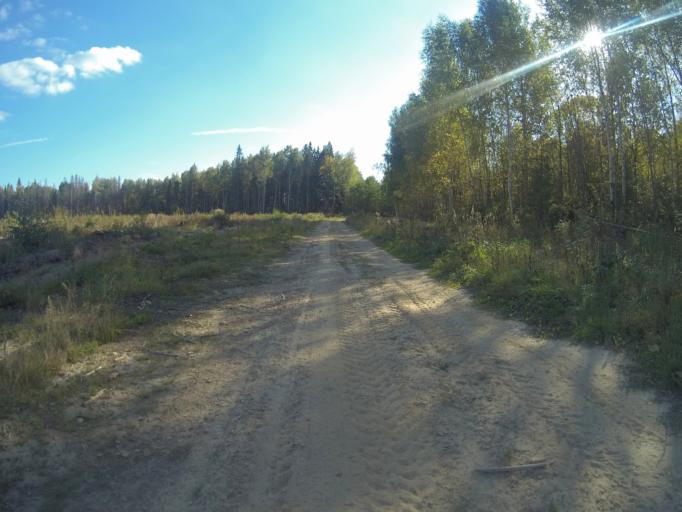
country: RU
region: Vladimir
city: Golovino
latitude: 55.9911
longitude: 40.4474
